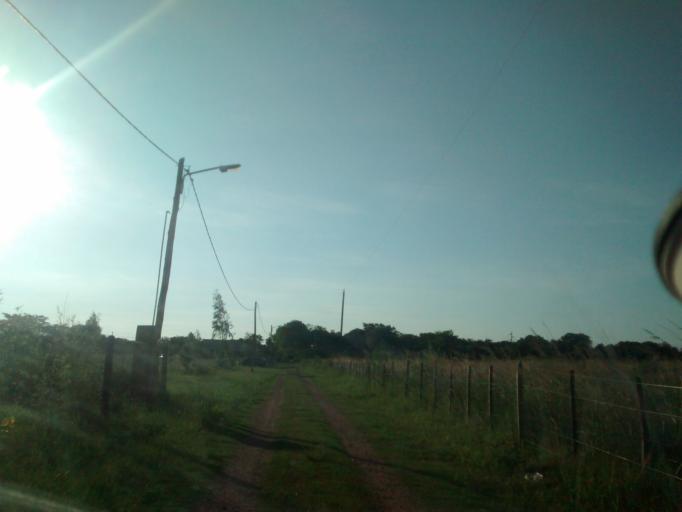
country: AR
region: Chaco
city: Colonia Benitez
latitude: -27.3077
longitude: -58.9891
